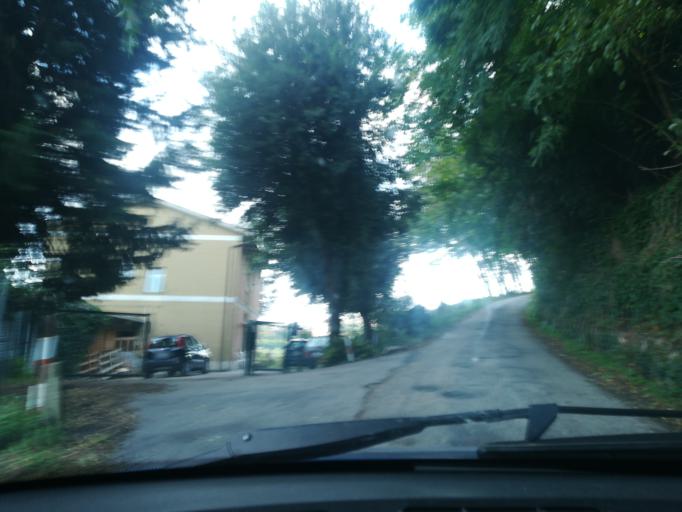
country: IT
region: The Marches
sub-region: Provincia di Macerata
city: Macerata
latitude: 43.3106
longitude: 13.4546
